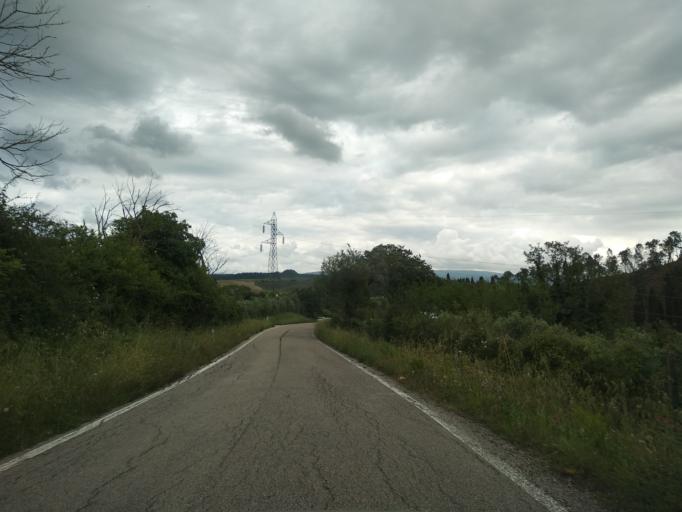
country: IT
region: Tuscany
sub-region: Provincia di Livorno
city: Collesalvetti
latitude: 43.5398
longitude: 10.4558
